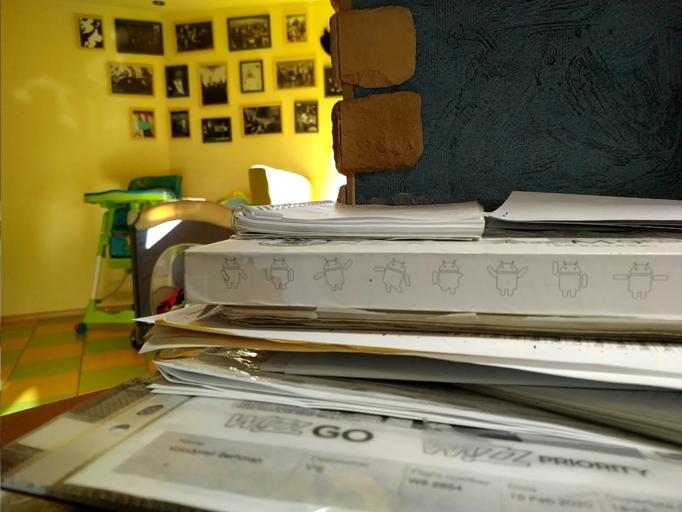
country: RU
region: Novgorod
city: Volot
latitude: 57.6159
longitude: 30.7846
